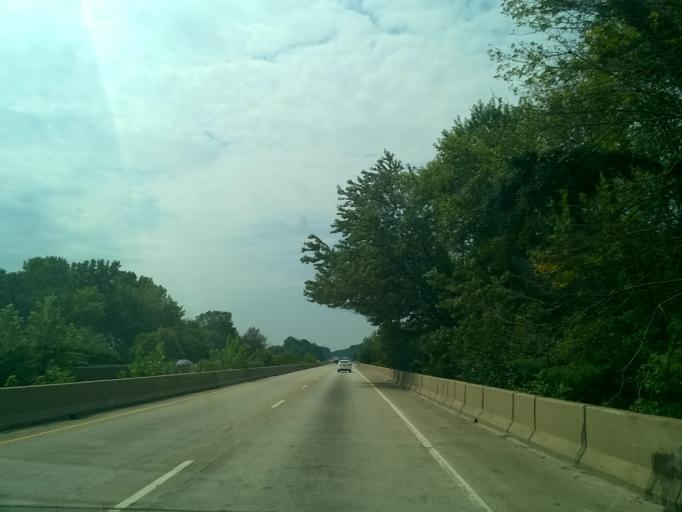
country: US
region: Indiana
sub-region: Putnam County
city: Cloverdale
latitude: 39.5030
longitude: -86.9565
